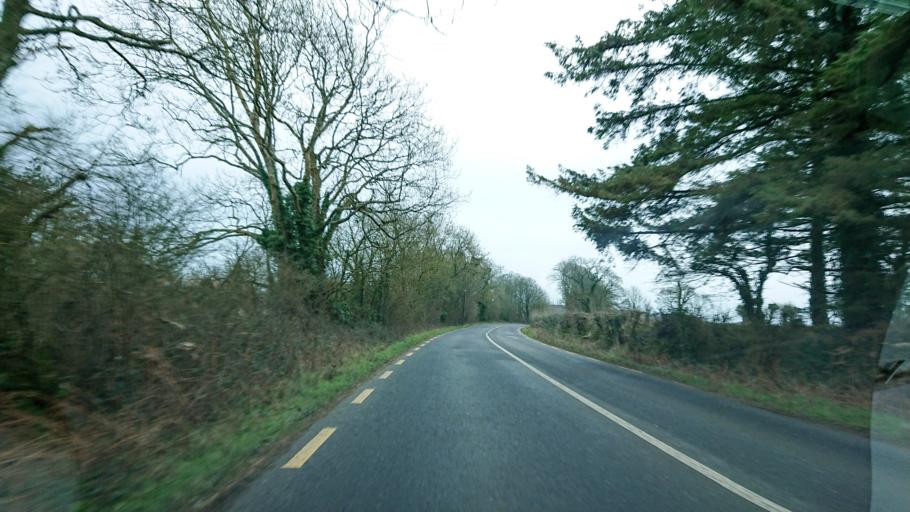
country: IE
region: Munster
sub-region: Waterford
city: Dunmore East
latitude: 52.2104
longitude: -7.0292
